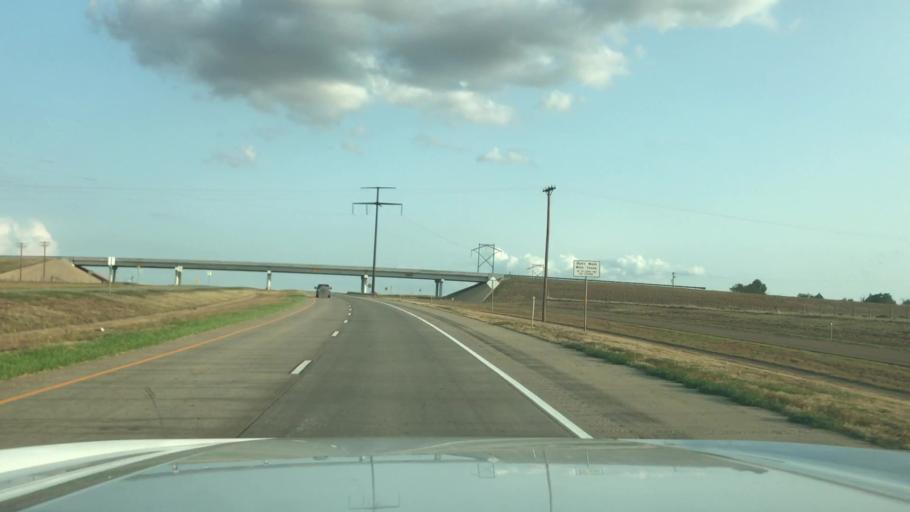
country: US
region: Texas
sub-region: Swisher County
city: Tulia
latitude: 34.5174
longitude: -101.7951
